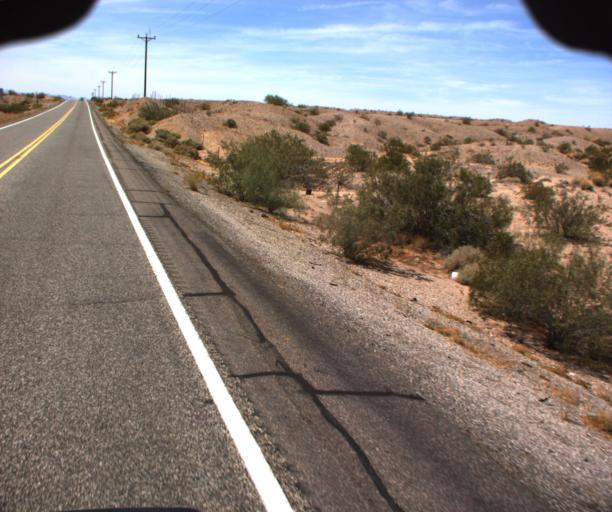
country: US
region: Arizona
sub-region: La Paz County
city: Parker
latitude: 34.0037
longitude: -114.2347
